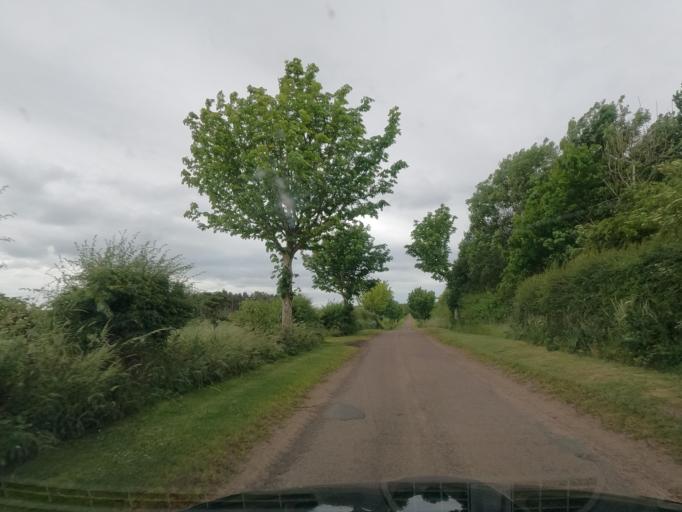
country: GB
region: England
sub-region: Northumberland
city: Ford
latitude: 55.6767
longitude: -2.1079
